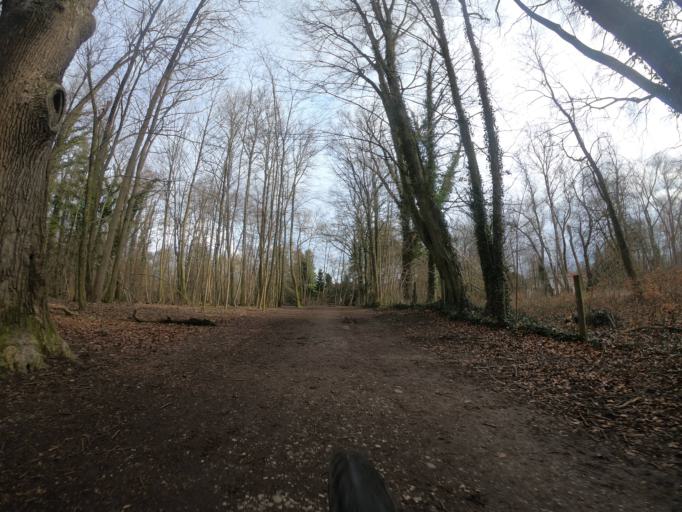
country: DE
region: Bavaria
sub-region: Upper Bavaria
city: Fuerstenfeldbruck
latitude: 48.1798
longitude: 11.2683
